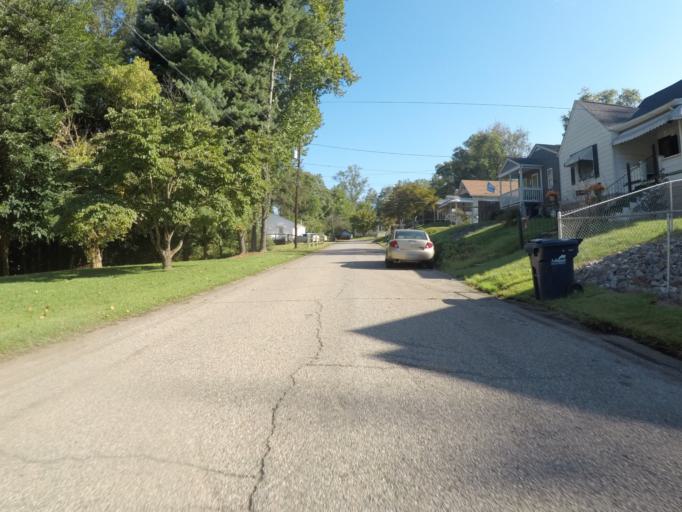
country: US
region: Kentucky
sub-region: Boyd County
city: Ashland
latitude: 38.4533
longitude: -82.6308
